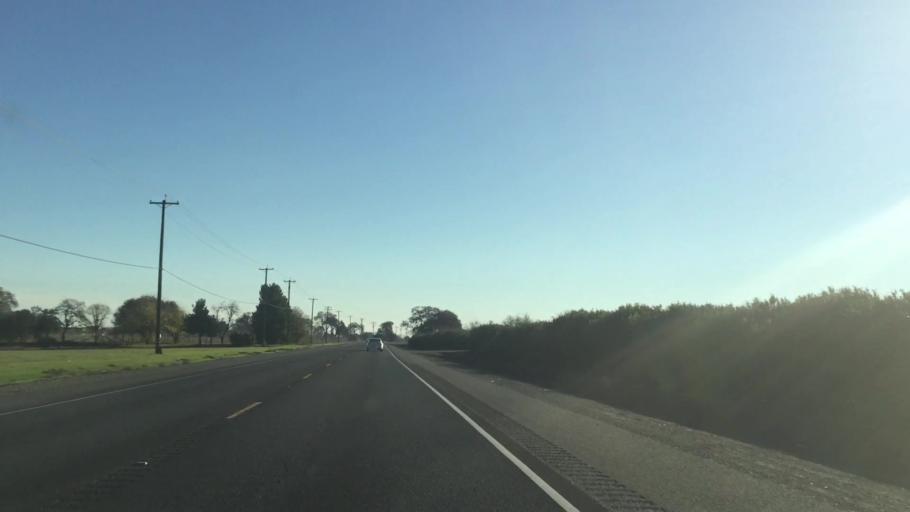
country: US
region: California
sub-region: Sutter County
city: Live Oak
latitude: 39.3408
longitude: -121.5997
